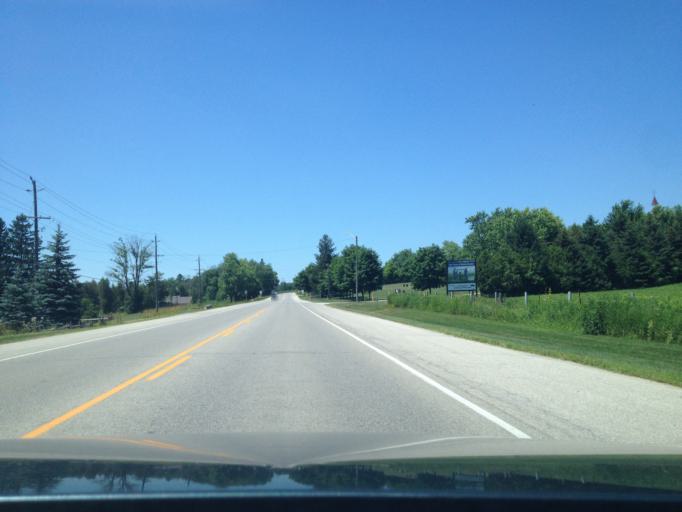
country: CA
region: Ontario
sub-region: Wellington County
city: Guelph
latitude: 43.6912
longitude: -80.3975
